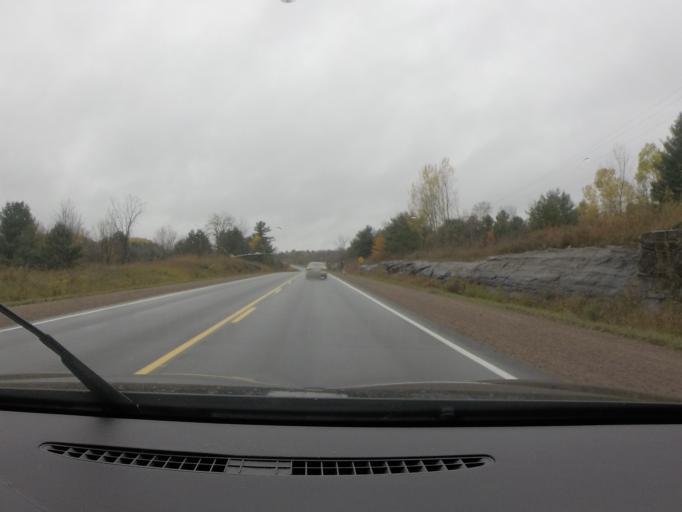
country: CA
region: Ontario
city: Skatepark
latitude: 44.7049
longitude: -77.0042
